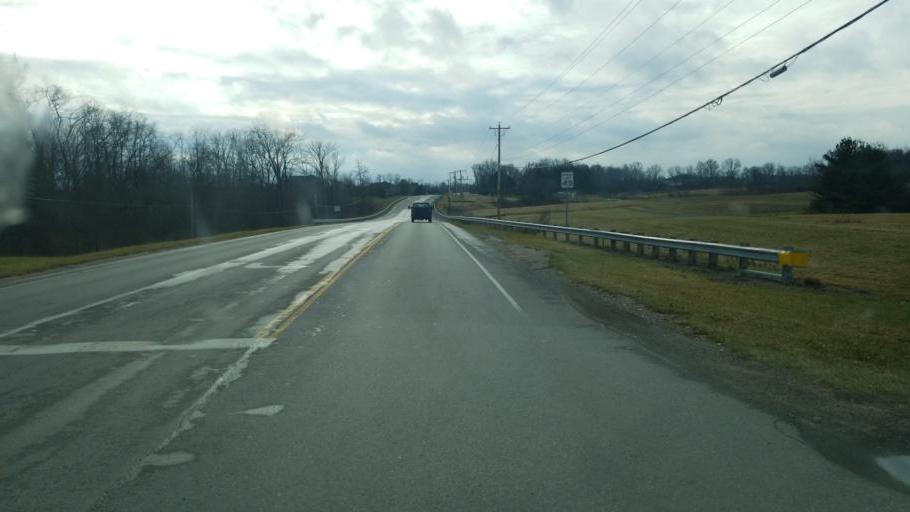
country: US
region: Ohio
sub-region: Delaware County
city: Powell
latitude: 40.1950
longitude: -83.0777
